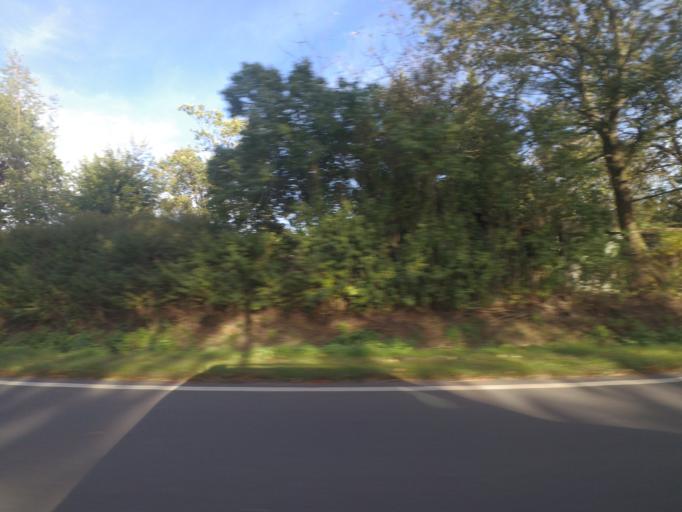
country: DE
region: Hesse
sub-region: Regierungsbezirk Kassel
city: Flieden
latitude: 50.4293
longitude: 9.5685
